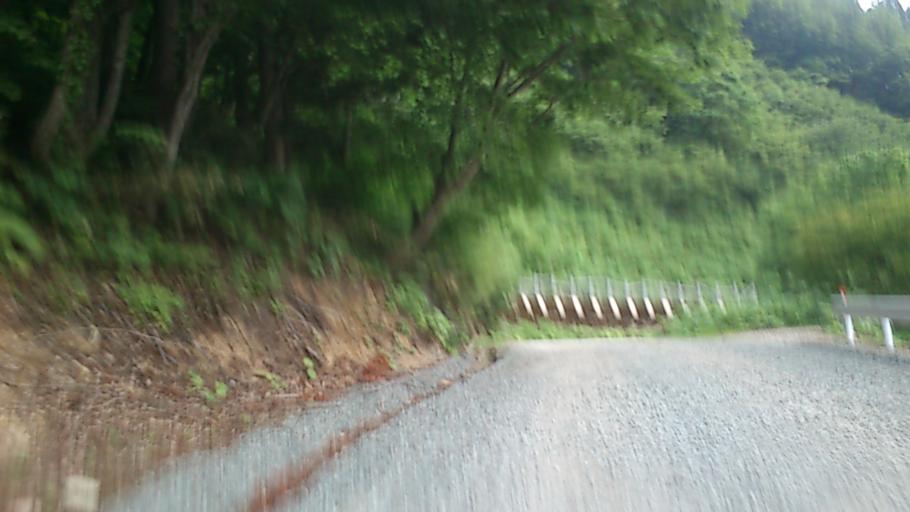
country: JP
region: Aomori
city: Hirosaki
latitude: 40.5266
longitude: 140.1789
